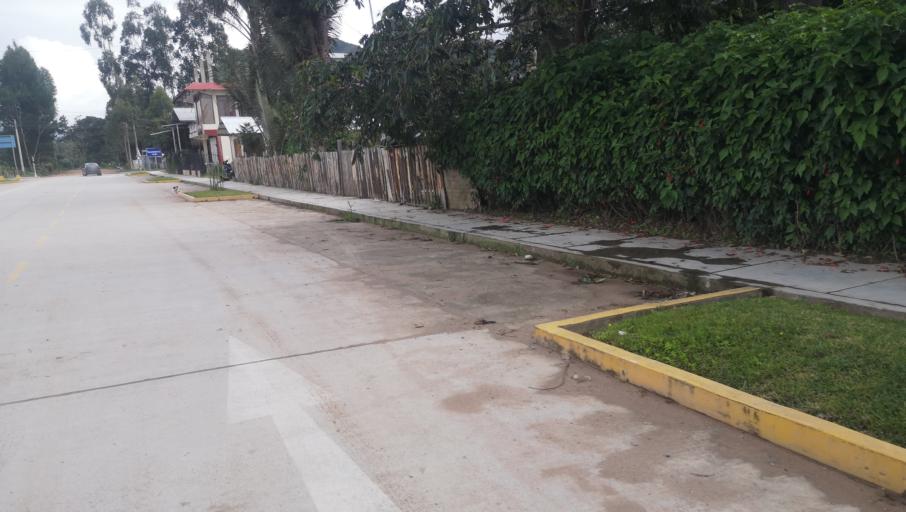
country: PE
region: Pasco
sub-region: Provincia de Oxapampa
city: Oxapampa
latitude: -10.5856
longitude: -75.4059
